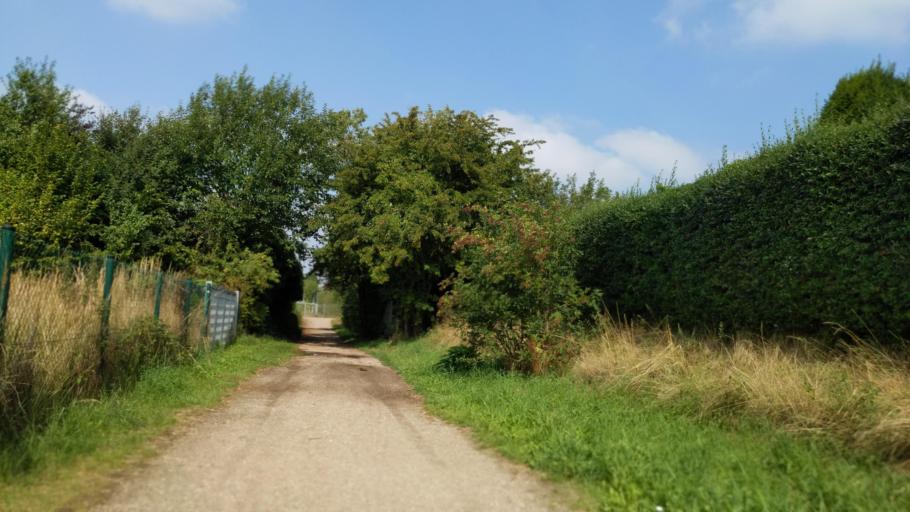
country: DE
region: Schleswig-Holstein
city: Stockelsdorf
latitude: 53.8905
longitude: 10.6306
